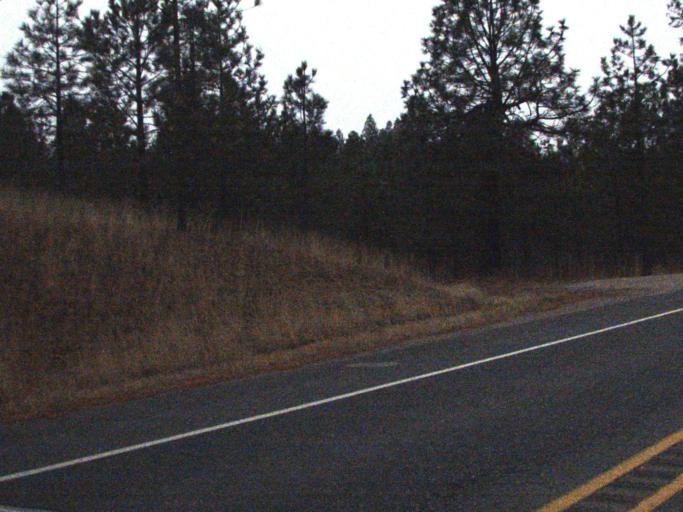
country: US
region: Washington
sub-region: Stevens County
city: Kettle Falls
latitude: 48.6068
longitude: -118.0812
